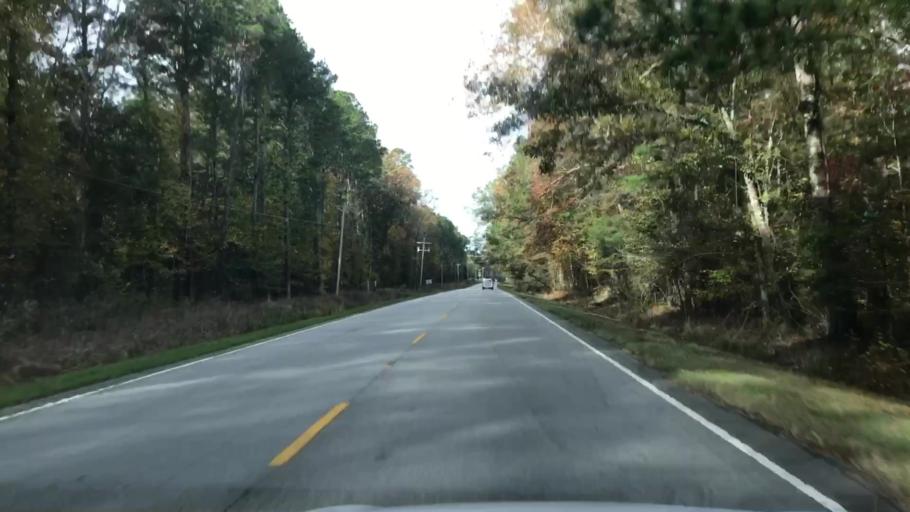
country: US
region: South Carolina
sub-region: Colleton County
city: Walterboro
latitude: 32.7996
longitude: -80.4983
